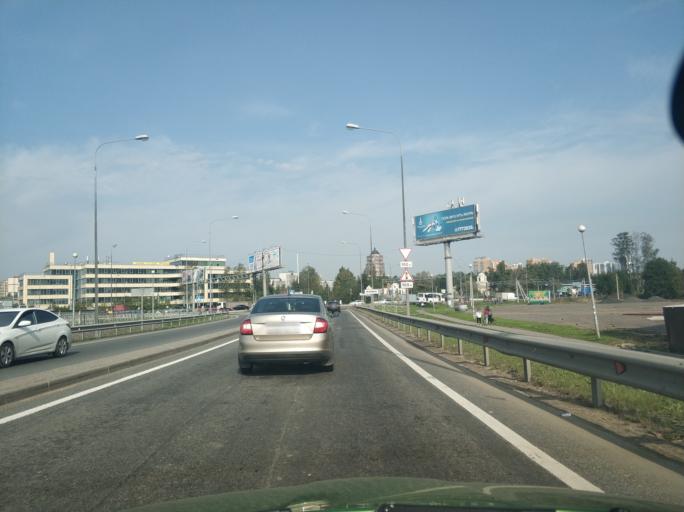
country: RU
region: Leningrad
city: Murino
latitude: 60.0409
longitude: 30.4439
